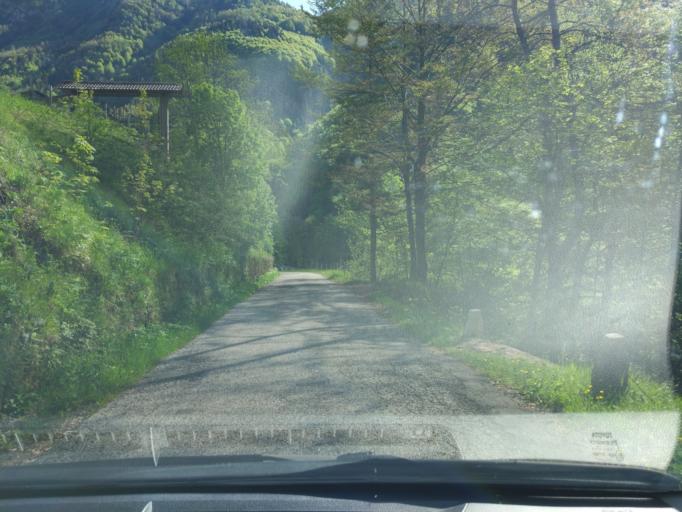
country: IT
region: Veneto
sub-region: Provincia di Verona
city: Selva di Progno
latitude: 45.6875
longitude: 11.1199
